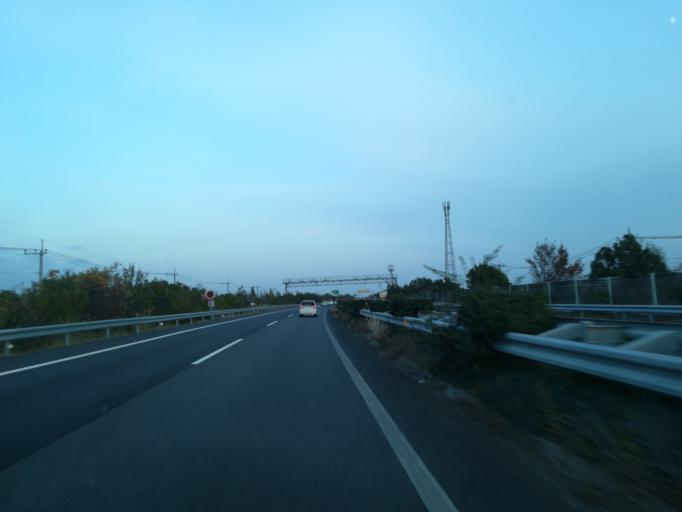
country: JP
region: Gunma
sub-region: Sawa-gun
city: Tamamura
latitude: 36.3331
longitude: 139.0871
